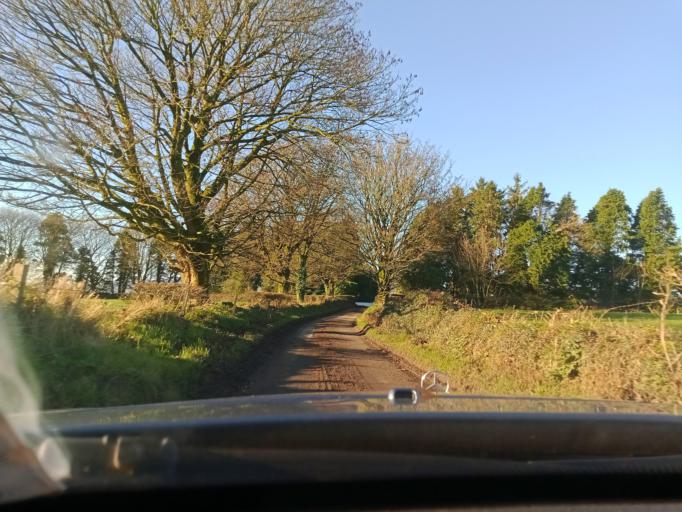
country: IE
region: Leinster
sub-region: Kilkenny
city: Callan
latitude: 52.4606
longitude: -7.4113
